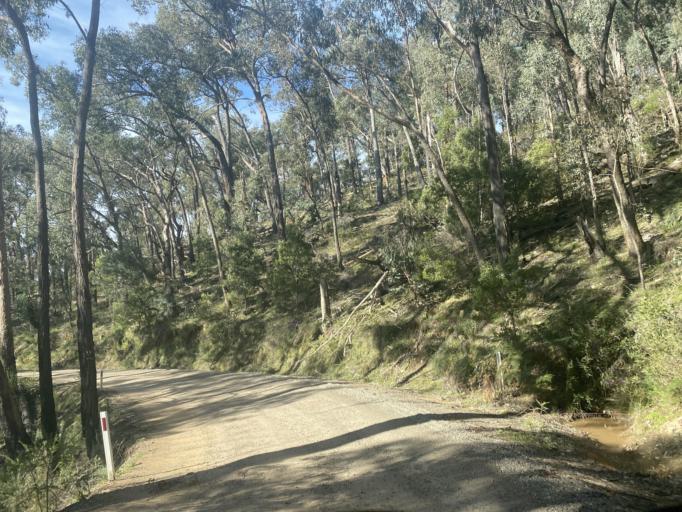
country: AU
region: Victoria
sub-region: Mansfield
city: Mansfield
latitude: -36.8398
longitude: 146.1647
